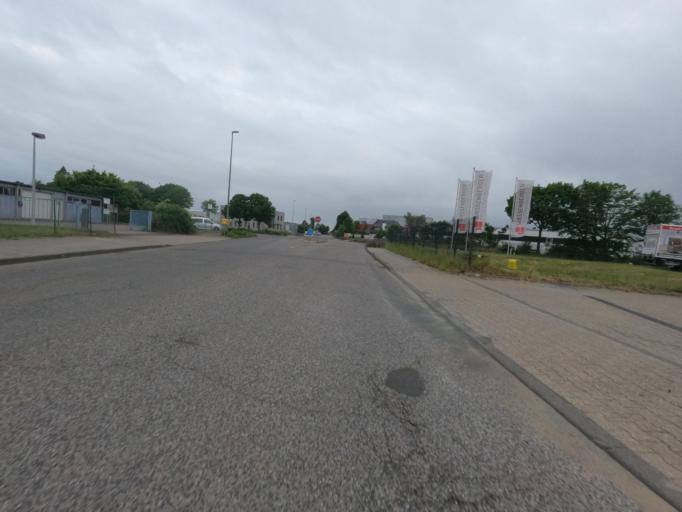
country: DE
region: North Rhine-Westphalia
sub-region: Regierungsbezirk Koln
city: Wassenberg
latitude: 51.1006
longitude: 6.1389
